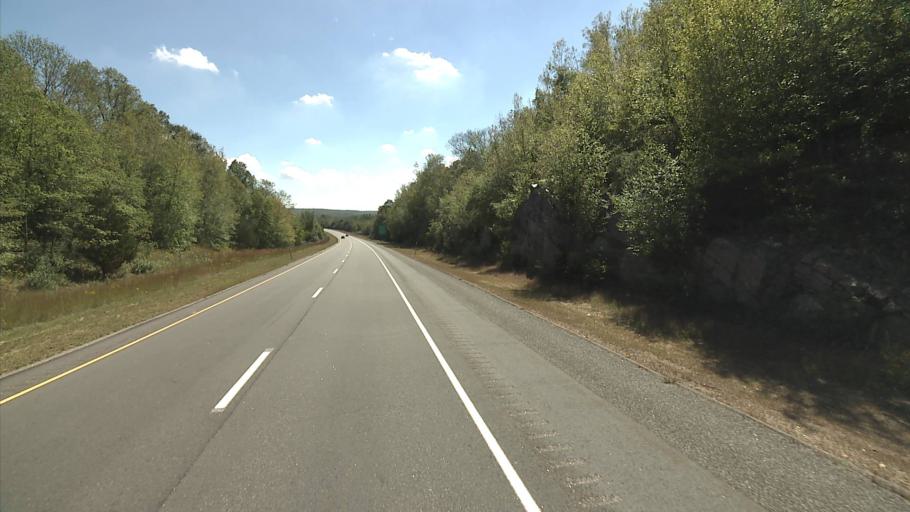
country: US
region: Connecticut
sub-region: New London County
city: Colchester
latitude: 41.4793
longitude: -72.2981
